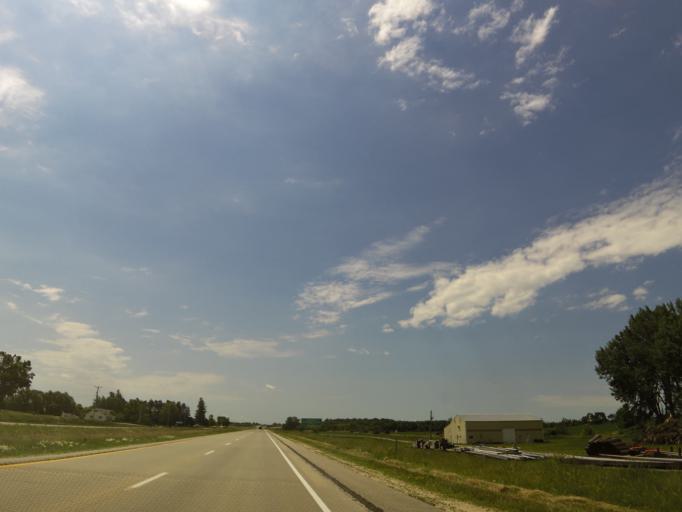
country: US
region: Iowa
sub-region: Bremer County
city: Denver
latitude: 42.7295
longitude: -92.3378
